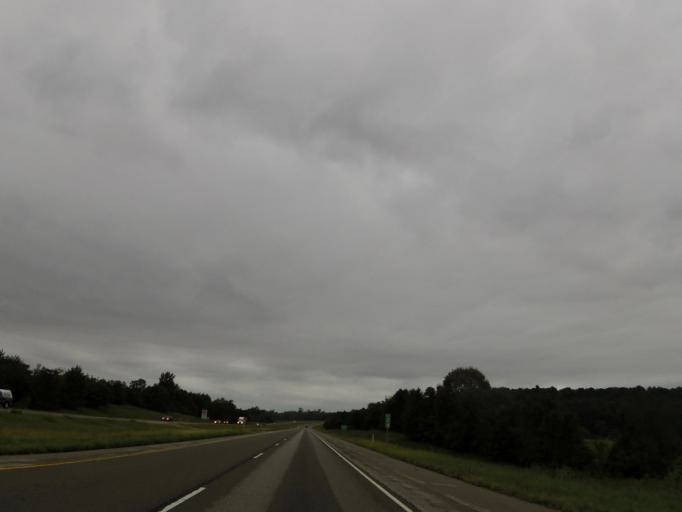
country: US
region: Illinois
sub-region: Johnson County
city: Vienna
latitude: 37.3341
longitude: -88.7786
